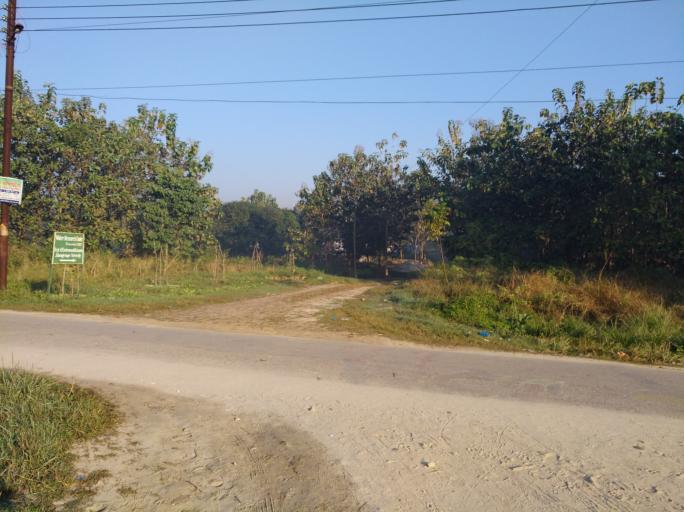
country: BD
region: Dhaka
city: Tungi
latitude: 23.8782
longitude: 90.2662
